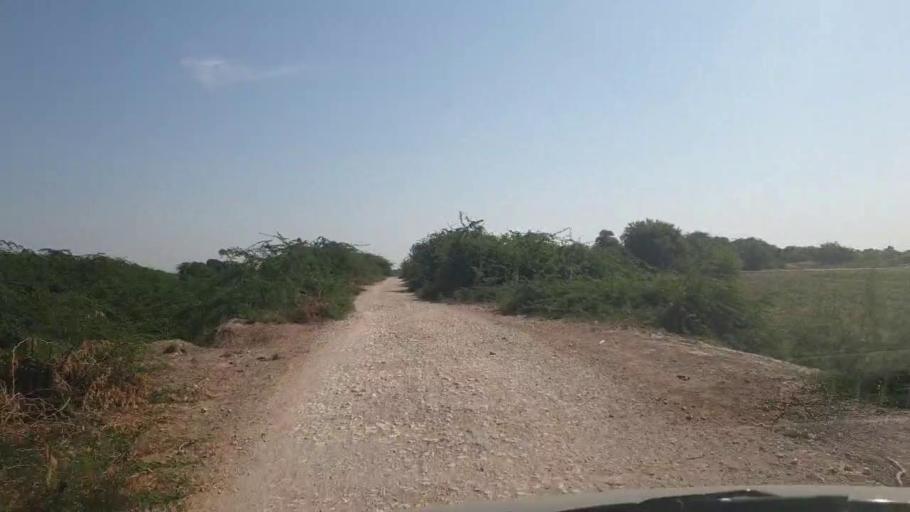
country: PK
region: Sindh
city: Digri
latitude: 24.9480
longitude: 69.1527
